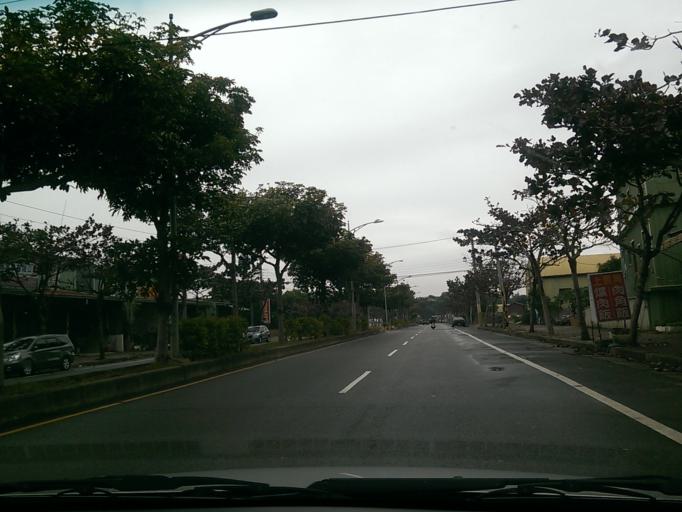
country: TW
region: Taiwan
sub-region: Taichung City
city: Taichung
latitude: 24.2176
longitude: 120.6148
